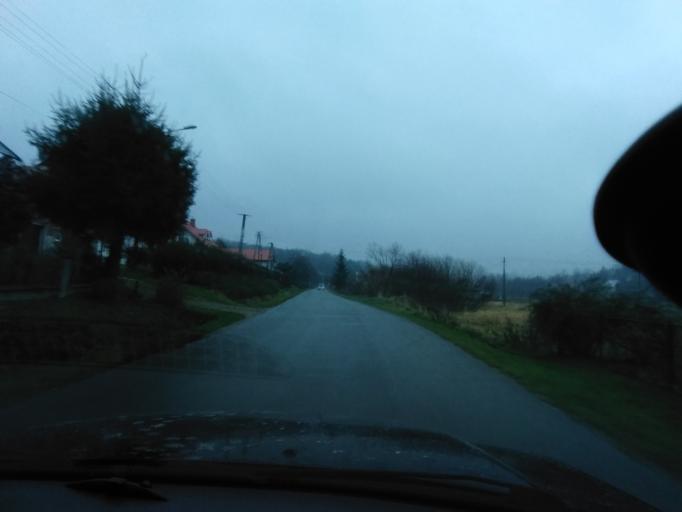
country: PL
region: Subcarpathian Voivodeship
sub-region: Powiat brzozowski
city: Jablonka
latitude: 49.7453
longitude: 22.1257
